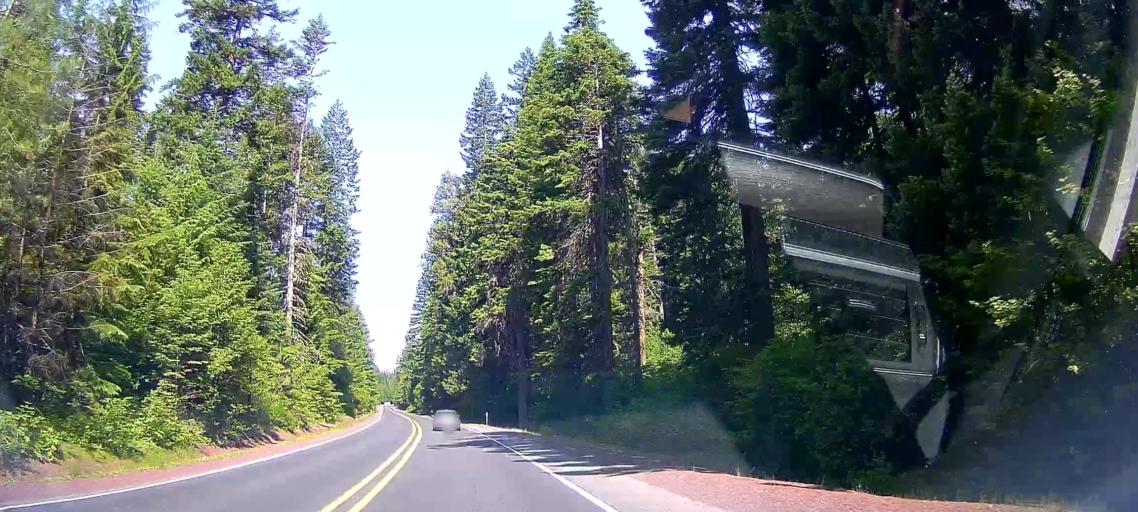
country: US
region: Oregon
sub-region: Jefferson County
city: Warm Springs
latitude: 45.1137
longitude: -121.5687
